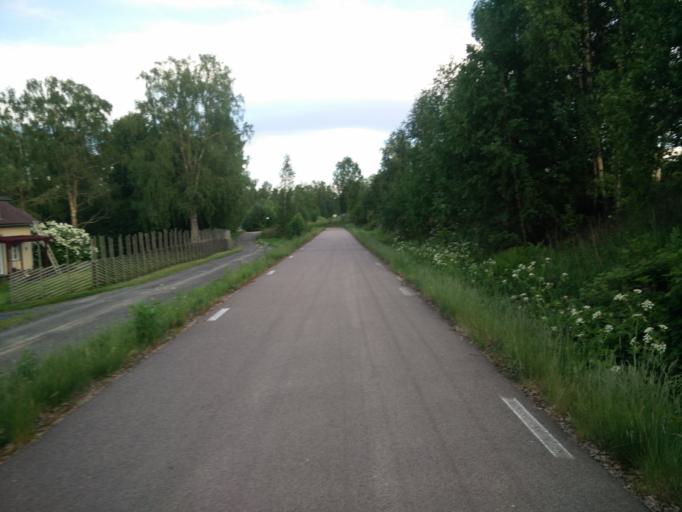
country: SE
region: Vaermland
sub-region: Hagfors Kommun
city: Hagfors
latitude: 60.0079
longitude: 13.6025
